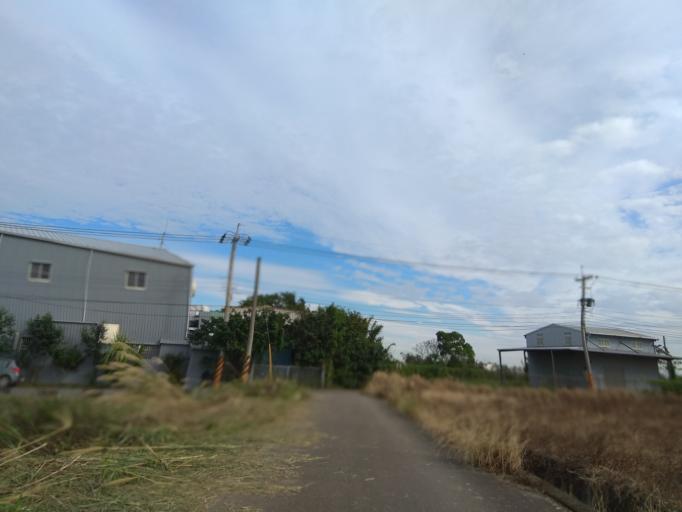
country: TW
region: Taiwan
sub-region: Hsinchu
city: Zhubei
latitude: 24.9593
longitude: 121.1042
